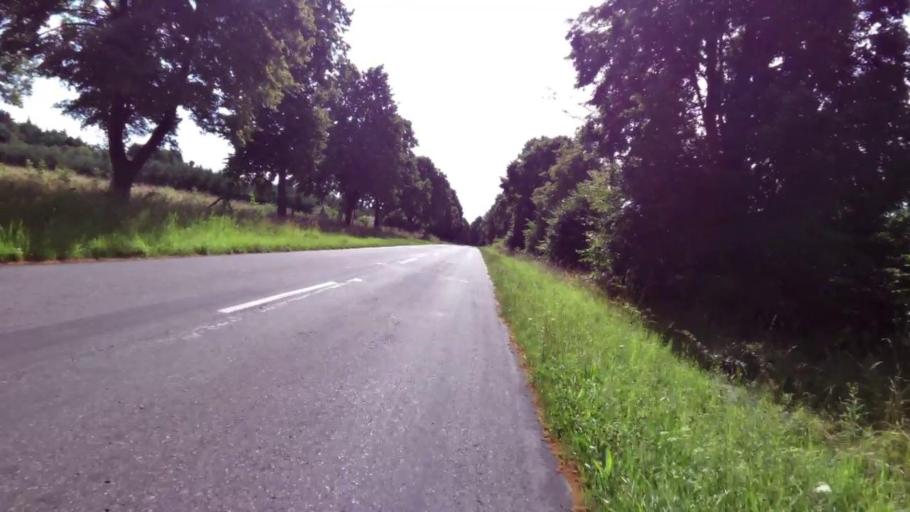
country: PL
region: West Pomeranian Voivodeship
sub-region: Powiat stargardzki
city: Dobrzany
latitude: 53.3708
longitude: 15.3735
